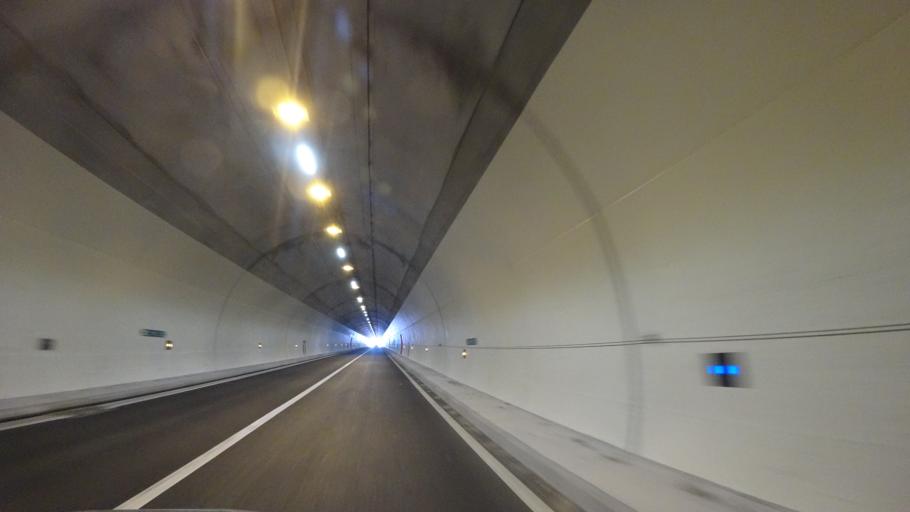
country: FR
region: Corsica
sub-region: Departement de la Corse-du-Sud
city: Propriano
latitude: 41.6714
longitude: 8.9273
